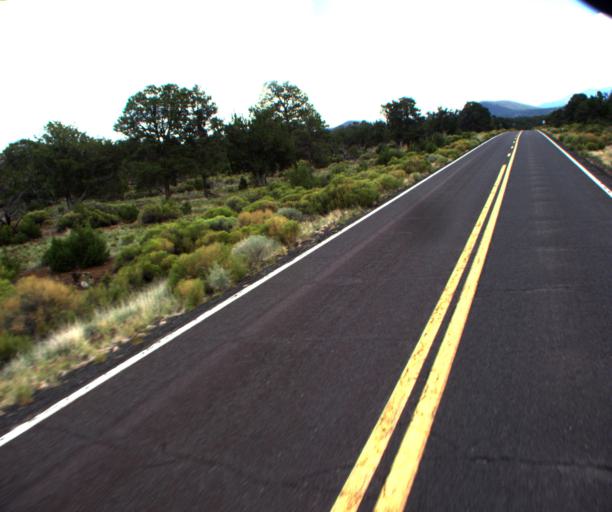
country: US
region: Arizona
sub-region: Coconino County
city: Parks
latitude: 35.5460
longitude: -111.8589
